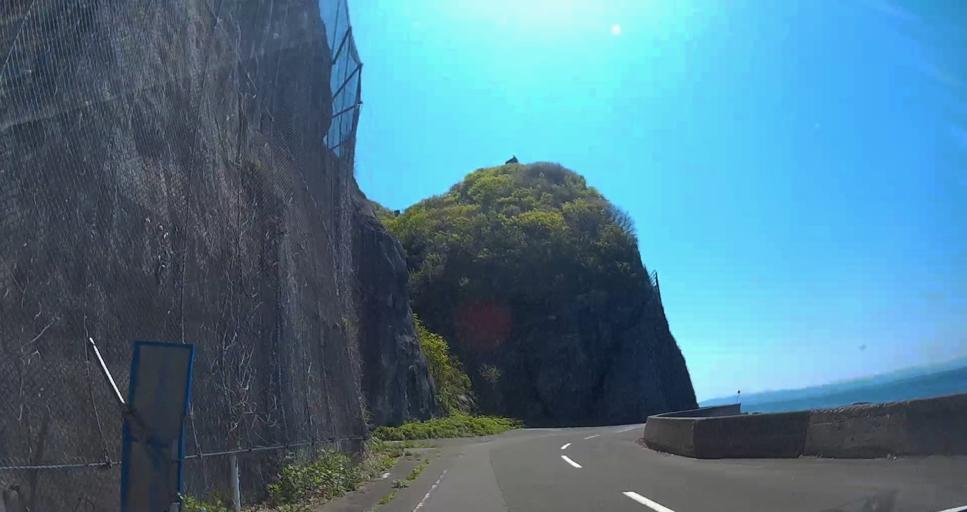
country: JP
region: Aomori
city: Aomori Shi
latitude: 41.1328
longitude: 140.7817
